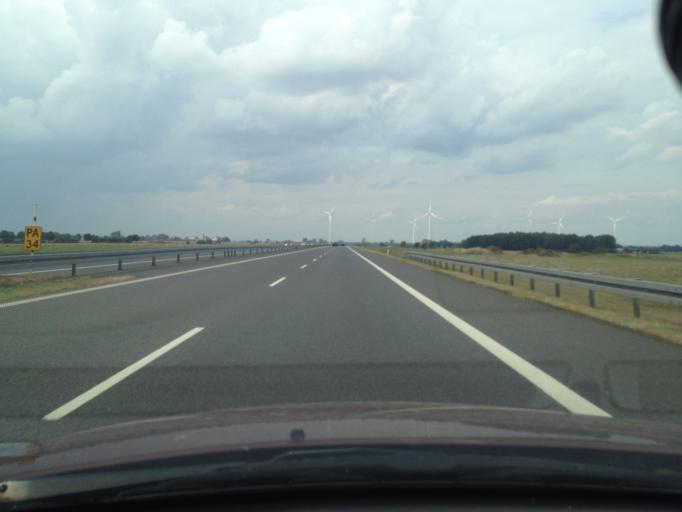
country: PL
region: West Pomeranian Voivodeship
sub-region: Powiat pyrzycki
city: Kozielice
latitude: 53.0902
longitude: 14.8338
